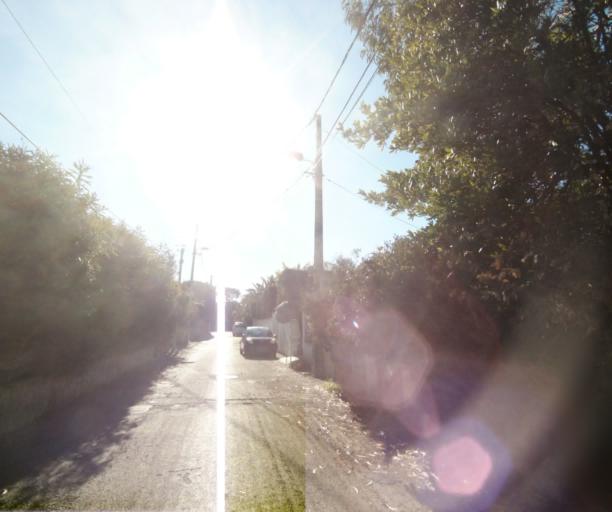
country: FR
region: Provence-Alpes-Cote d'Azur
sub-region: Departement des Alpes-Maritimes
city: Antibes
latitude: 43.5683
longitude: 7.1223
